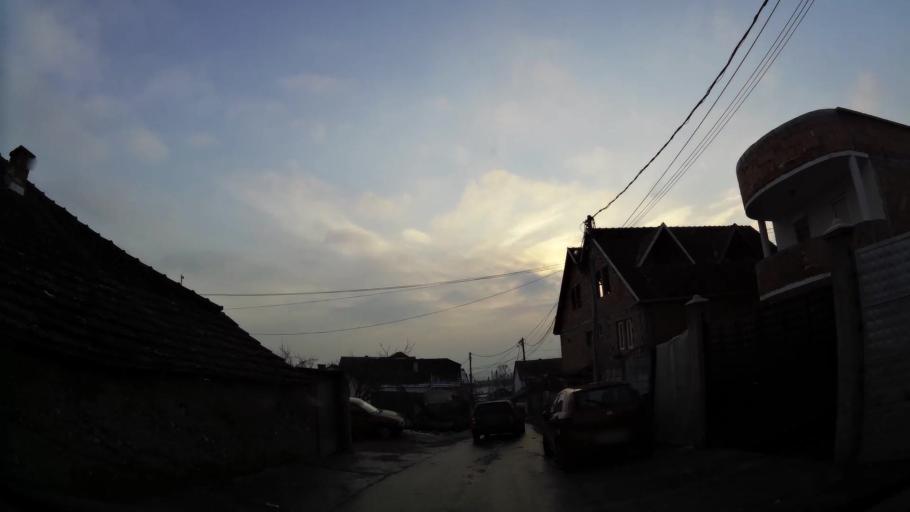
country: MK
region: Aracinovo
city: Arachinovo
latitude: 42.0251
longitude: 21.5617
